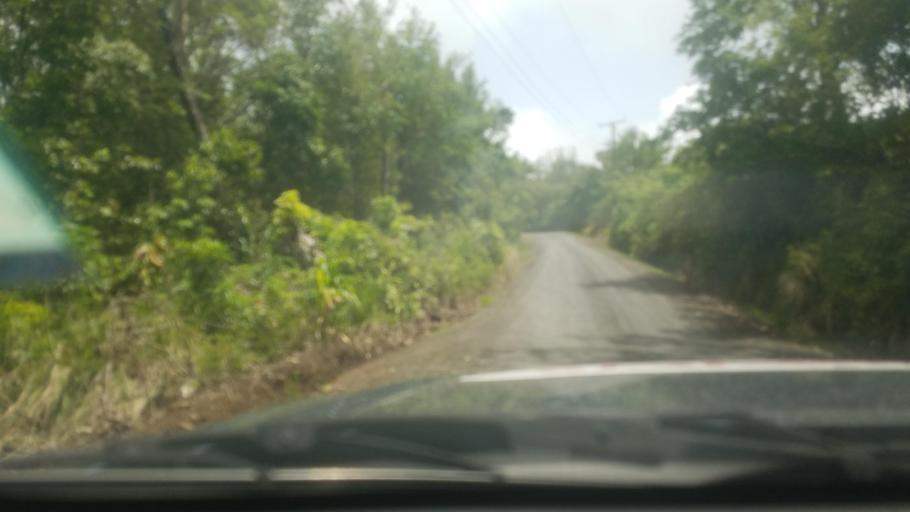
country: LC
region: Laborie Quarter
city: Laborie
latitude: 13.7578
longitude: -60.9941
